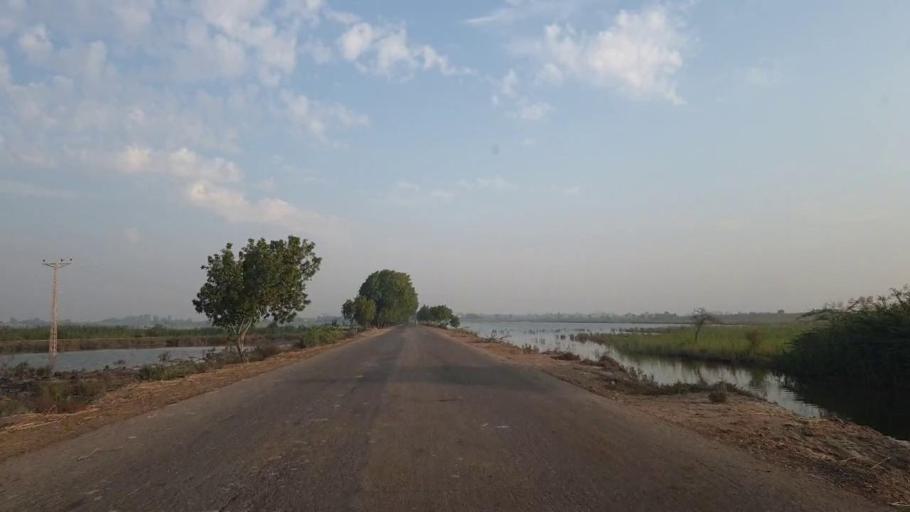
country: PK
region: Sindh
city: Tando Bago
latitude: 24.7446
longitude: 68.9482
